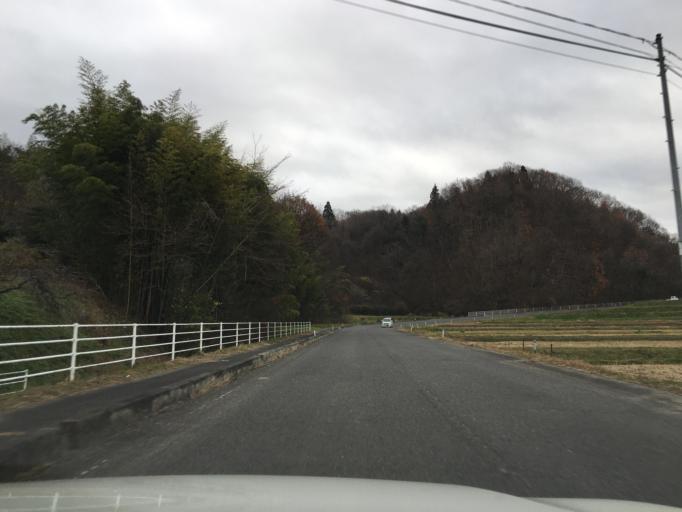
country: JP
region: Fukushima
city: Funehikimachi-funehiki
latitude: 37.4751
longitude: 140.5478
